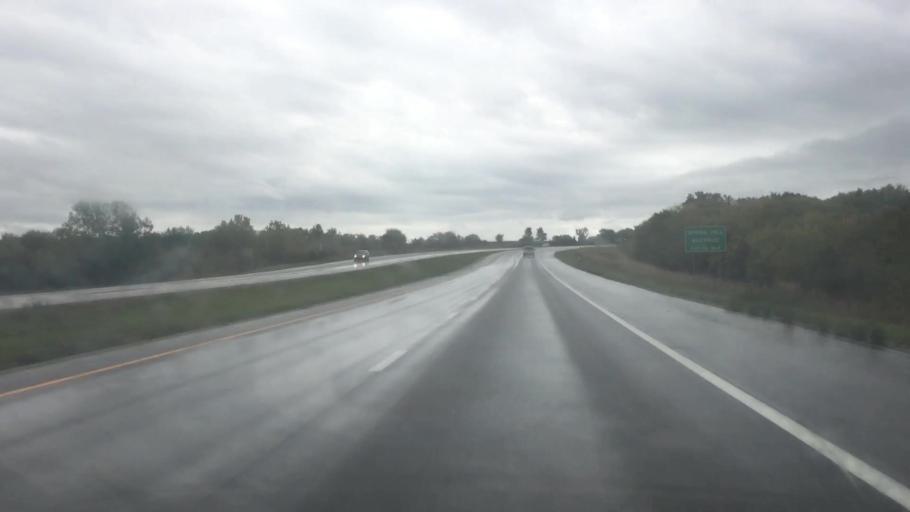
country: US
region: Kansas
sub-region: Johnson County
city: Spring Hill
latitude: 38.7336
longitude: -94.8368
